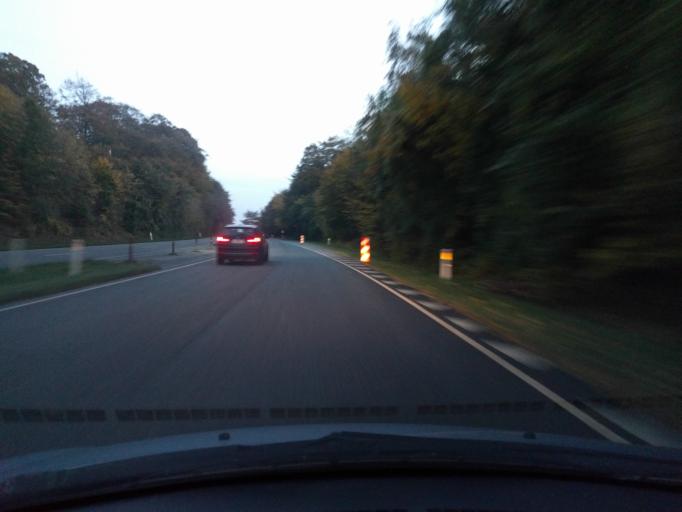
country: DK
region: South Denmark
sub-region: Svendborg Kommune
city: Svendborg
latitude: 55.0558
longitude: 10.5912
